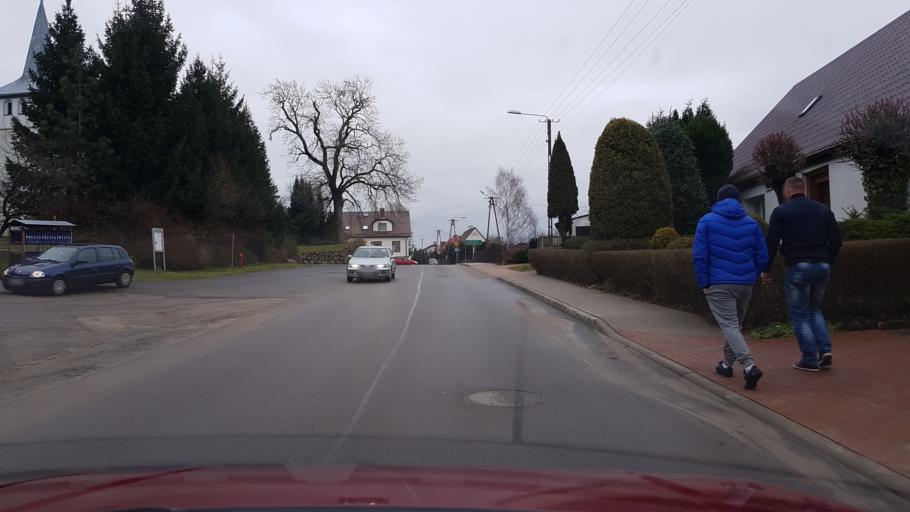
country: PL
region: West Pomeranian Voivodeship
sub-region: Powiat koszalinski
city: Mielno
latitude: 54.1335
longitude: 16.0374
